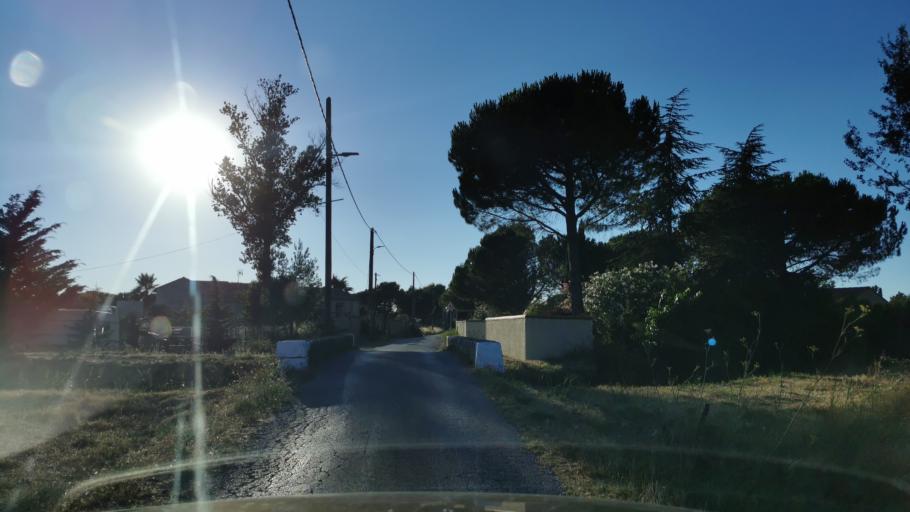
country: FR
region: Languedoc-Roussillon
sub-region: Departement de l'Aude
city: Coursan
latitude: 43.2665
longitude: 3.0184
